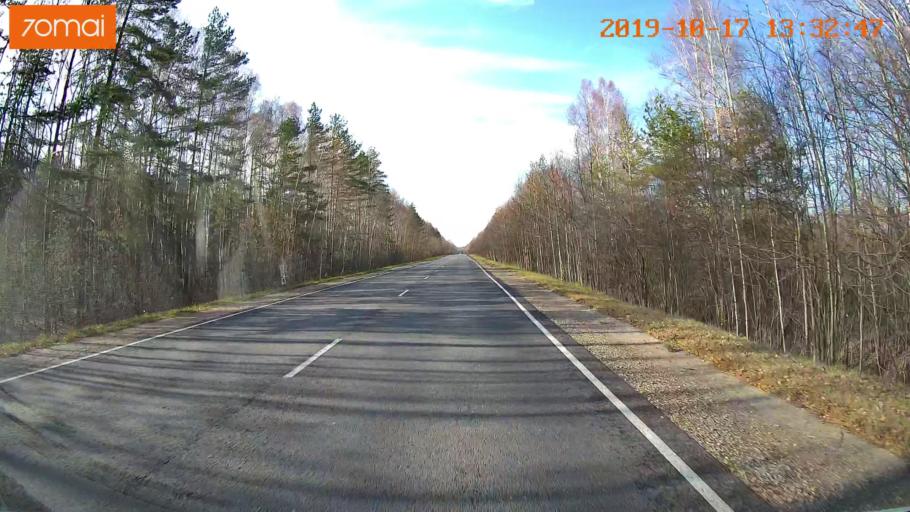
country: RU
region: Vladimir
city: Velikodvorskiy
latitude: 55.1389
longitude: 40.7569
